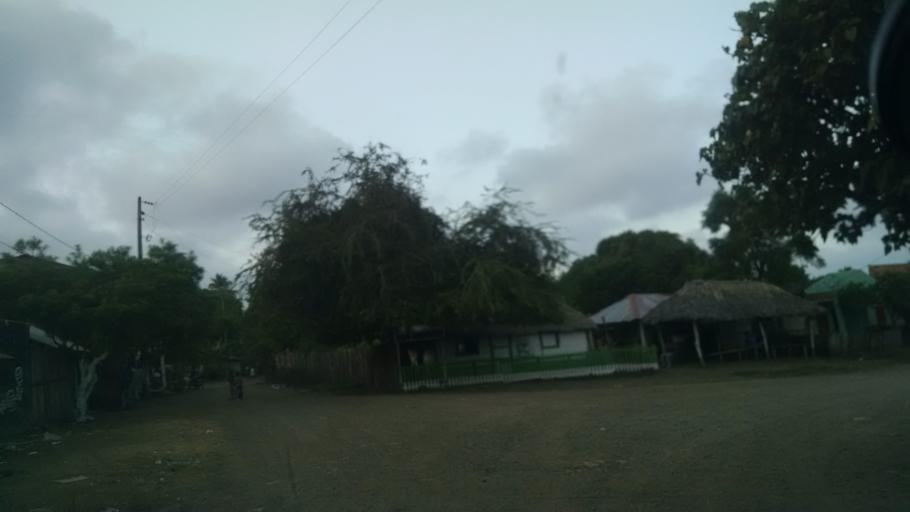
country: CO
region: Antioquia
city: San Juan de Uraba
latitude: 8.7362
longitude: -76.6073
